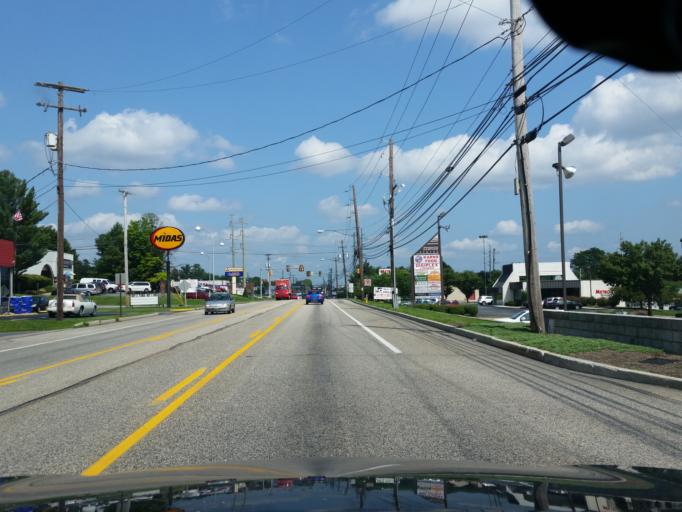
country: US
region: Pennsylvania
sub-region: Cumberland County
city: Shiremanstown
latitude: 40.2373
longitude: -76.9691
